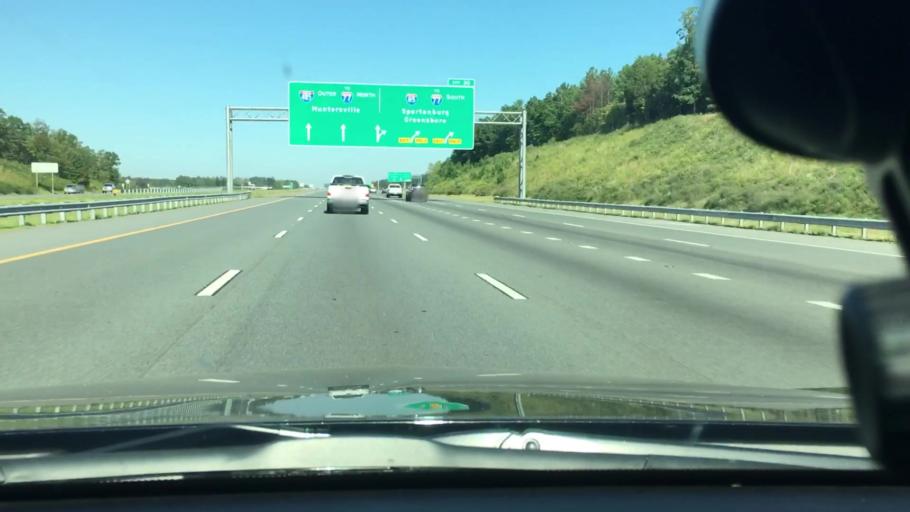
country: US
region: North Carolina
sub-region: Cabarrus County
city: Harrisburg
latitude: 35.3405
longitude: -80.7269
